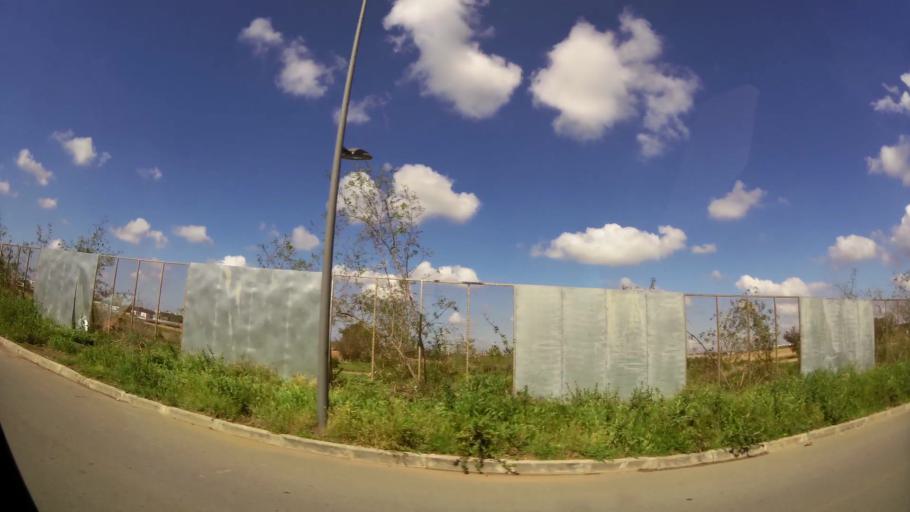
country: MA
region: Grand Casablanca
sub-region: Nouaceur
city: Bouskoura
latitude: 33.4747
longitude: -7.6180
